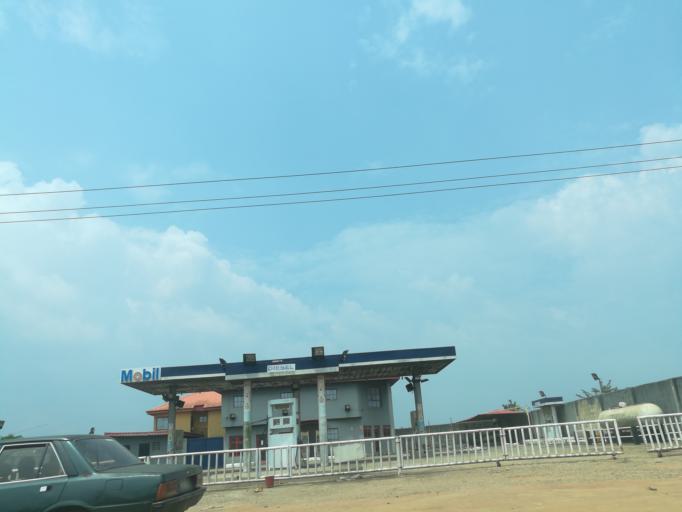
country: NG
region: Lagos
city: Ikorodu
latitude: 6.6067
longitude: 3.5959
